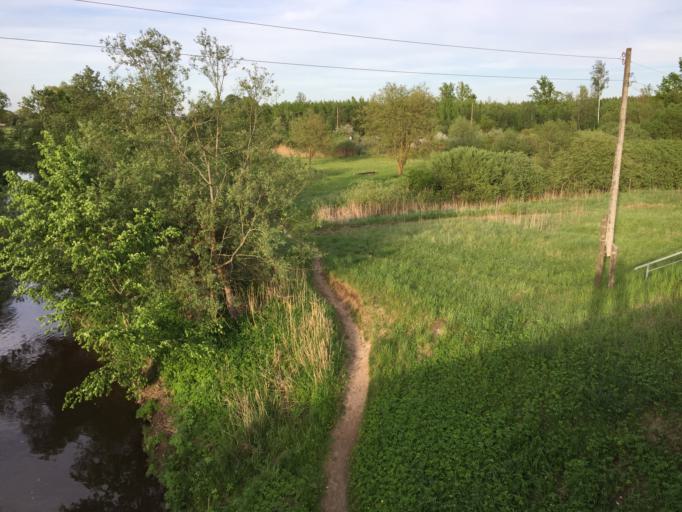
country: LV
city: Tireli
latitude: 56.6818
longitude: 23.4983
